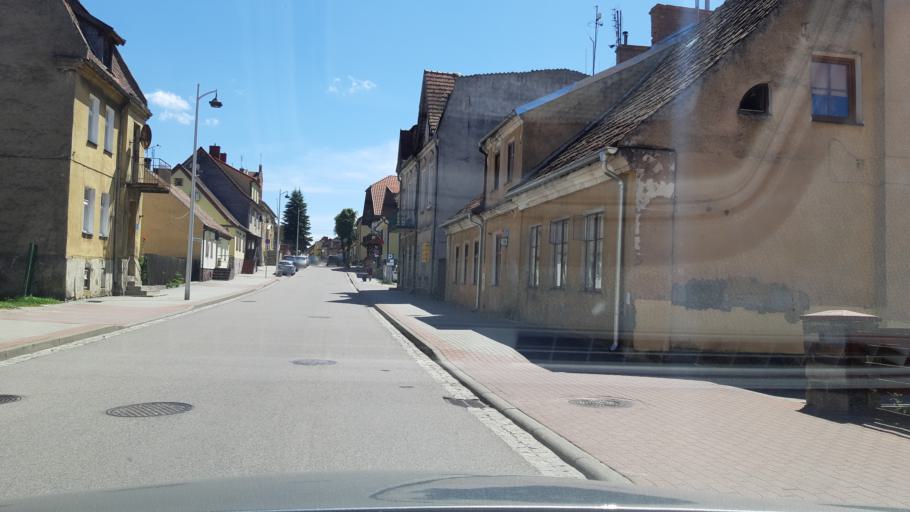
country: PL
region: Warmian-Masurian Voivodeship
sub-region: Powiat mragowski
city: Mikolajki
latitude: 53.7996
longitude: 21.5745
